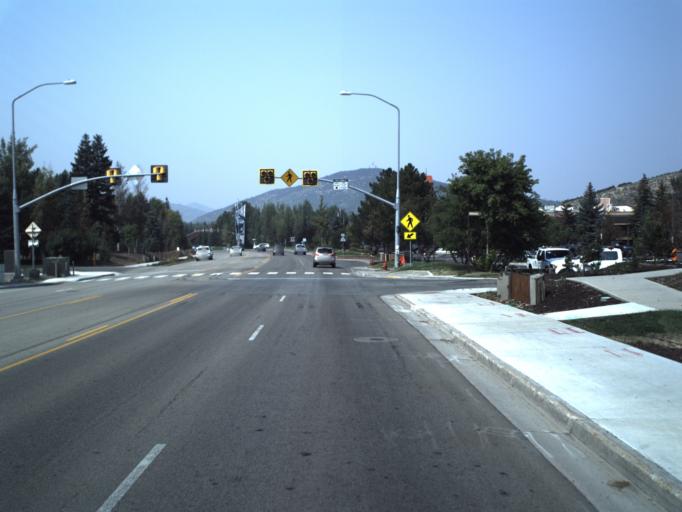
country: US
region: Utah
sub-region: Summit County
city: Park City
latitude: 40.6584
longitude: -111.5076
